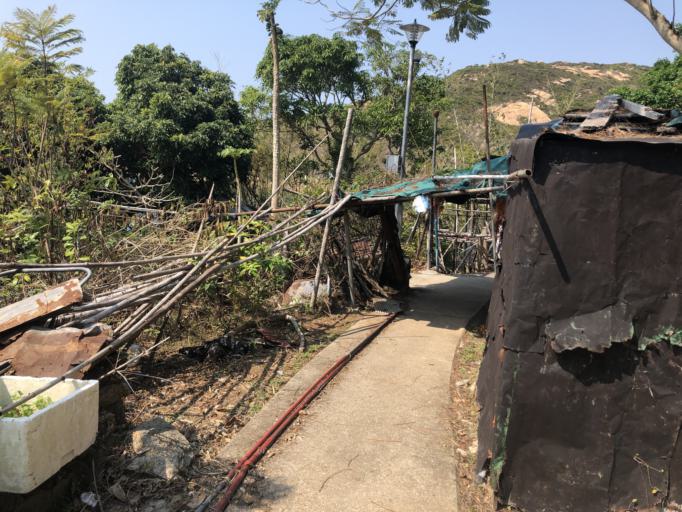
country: HK
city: Sok Kwu Wan
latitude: 22.1637
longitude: 114.2540
